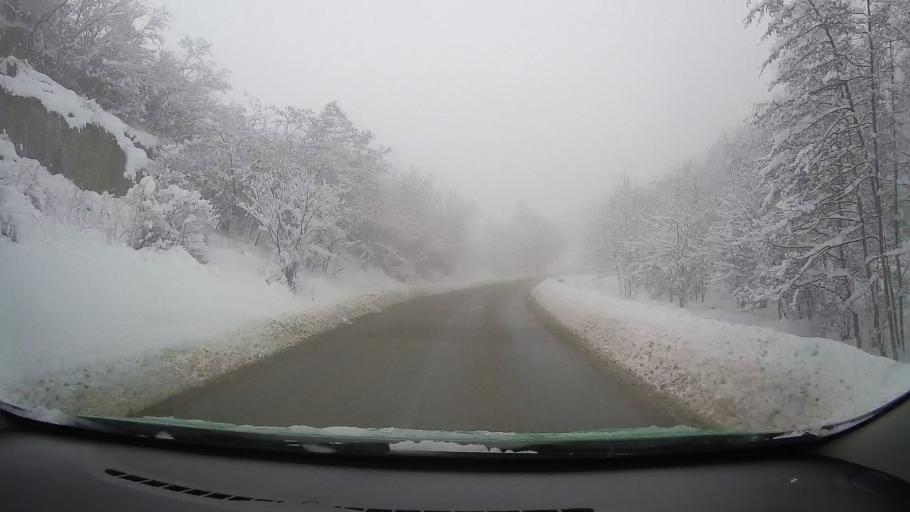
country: RO
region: Sibiu
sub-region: Comuna Poiana Sibiului
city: Poiana Sibiului
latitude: 45.8078
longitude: 23.7695
